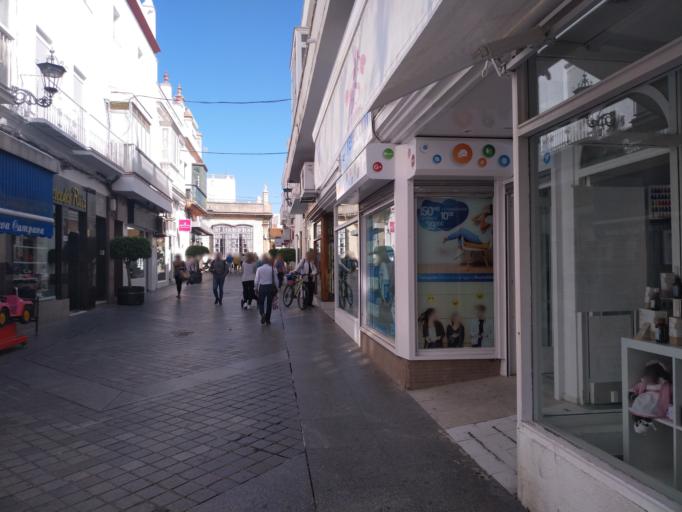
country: ES
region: Andalusia
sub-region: Provincia de Cadiz
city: San Fernando
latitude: 36.4678
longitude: -6.1960
